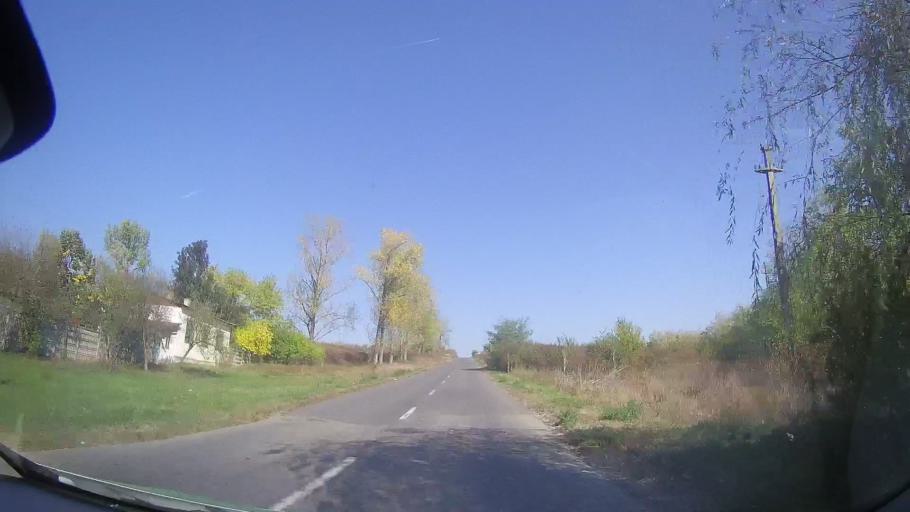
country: RO
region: Timis
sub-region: Comuna Costeiu
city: Costeiu
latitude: 45.7559
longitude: 21.8479
